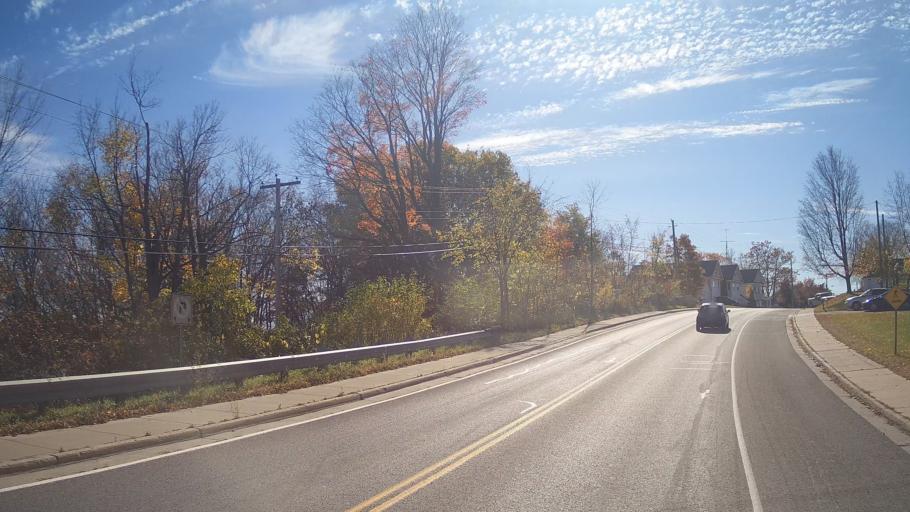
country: CA
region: Ontario
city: Perth
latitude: 44.7743
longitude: -76.6847
